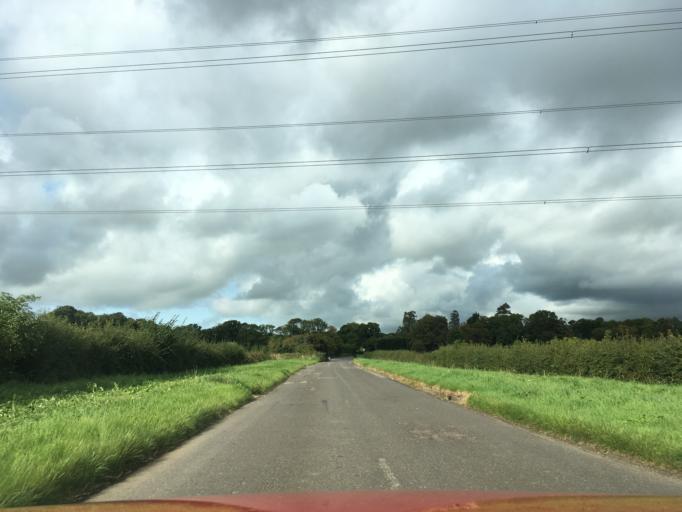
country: GB
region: England
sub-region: South Gloucestershire
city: Tytherington
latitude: 51.6182
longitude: -2.4830
